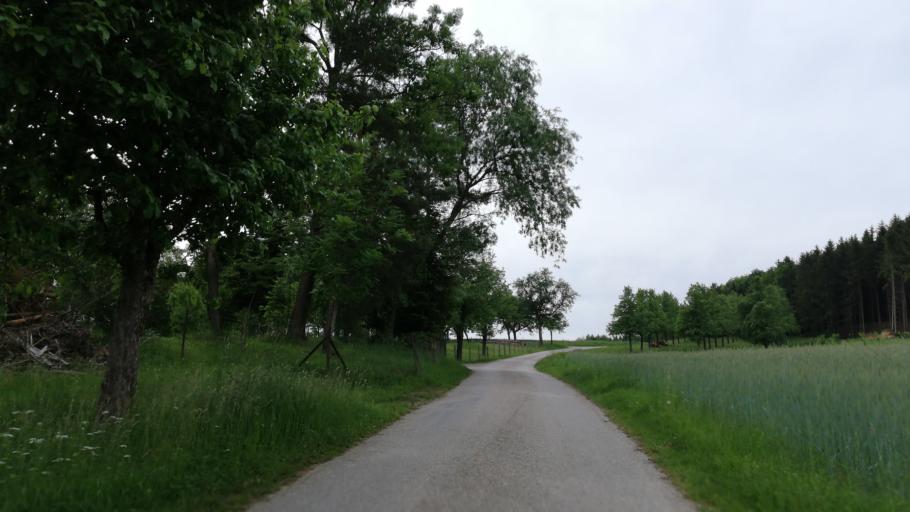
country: AT
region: Upper Austria
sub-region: Wels-Land
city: Gunskirchen
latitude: 48.1714
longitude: 13.9345
